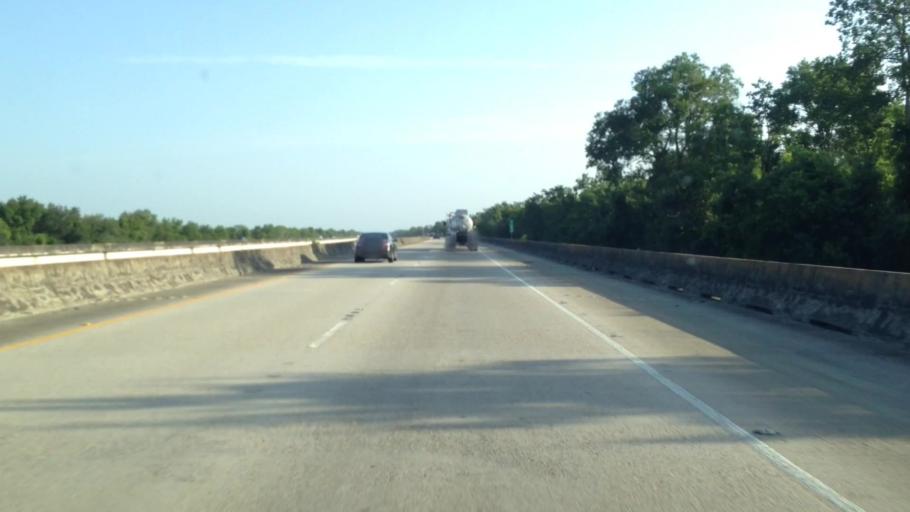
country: US
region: Louisiana
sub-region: Tangipahoa Parish
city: Ponchatoula
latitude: 30.3349
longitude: -90.4115
